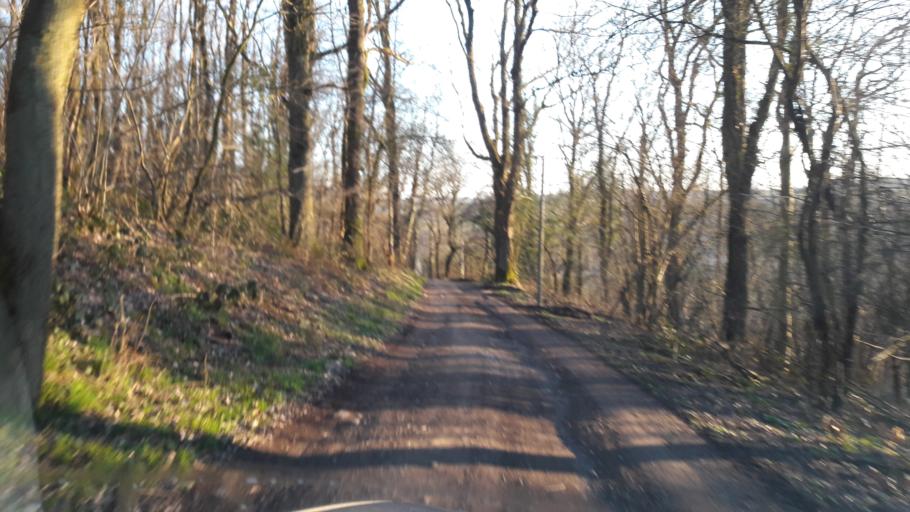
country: BE
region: Wallonia
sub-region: Province du Hainaut
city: Beaumont
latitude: 50.2463
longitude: 4.1856
